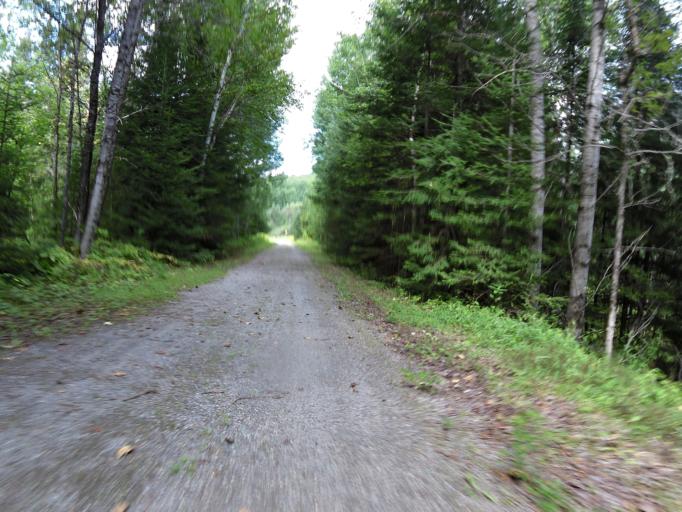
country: CA
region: Quebec
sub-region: Outaouais
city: Wakefield
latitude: 45.8417
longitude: -75.9786
